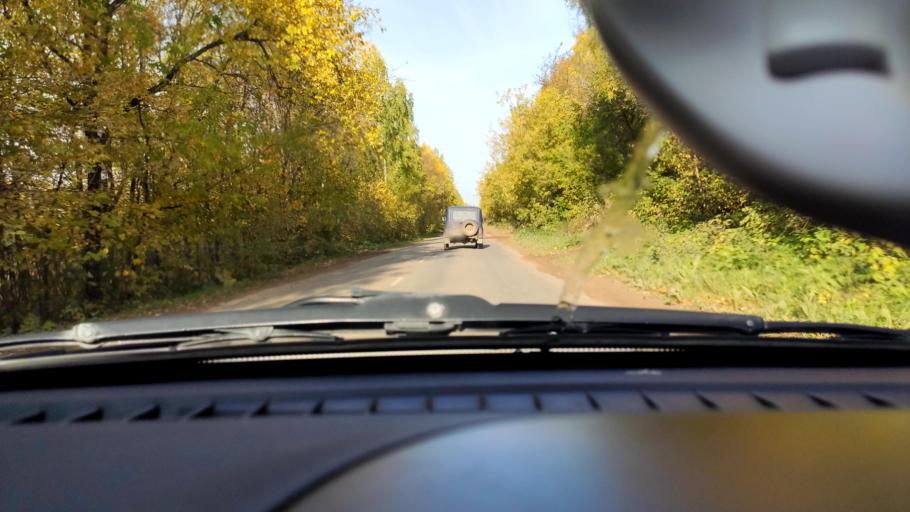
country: RU
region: Perm
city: Overyata
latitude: 58.0650
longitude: 55.8895
